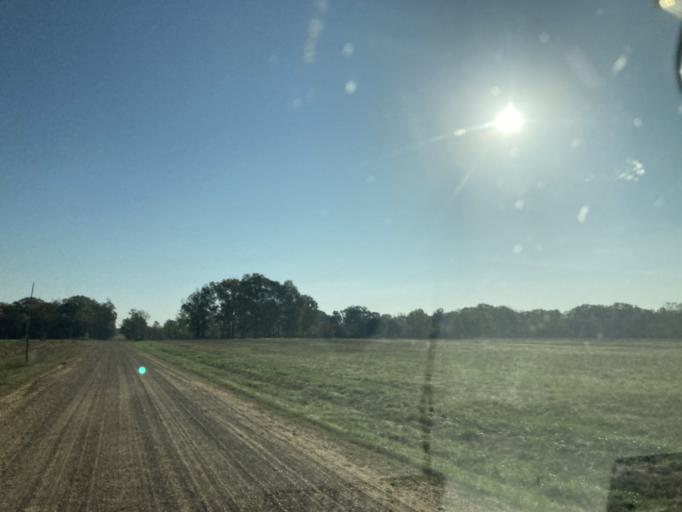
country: US
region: Mississippi
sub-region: Madison County
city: Kearney Park
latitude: 32.7058
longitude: -90.2492
